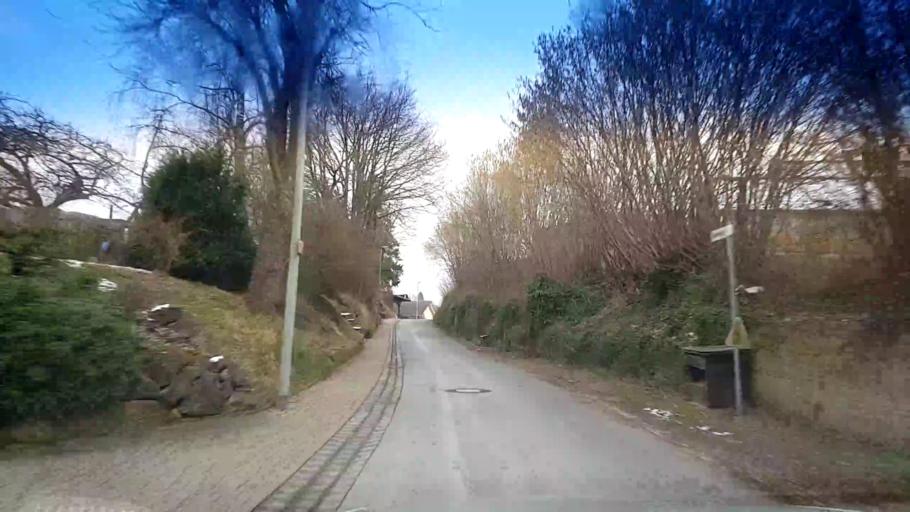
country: DE
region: Bavaria
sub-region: Upper Franconia
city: Pommersfelden
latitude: 49.8173
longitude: 10.8068
